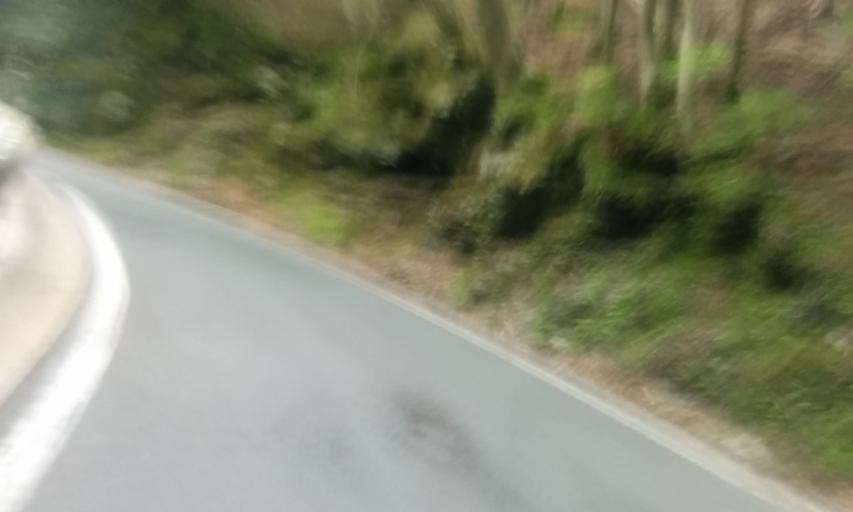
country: JP
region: Ehime
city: Saijo
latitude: 33.8020
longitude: 133.2796
